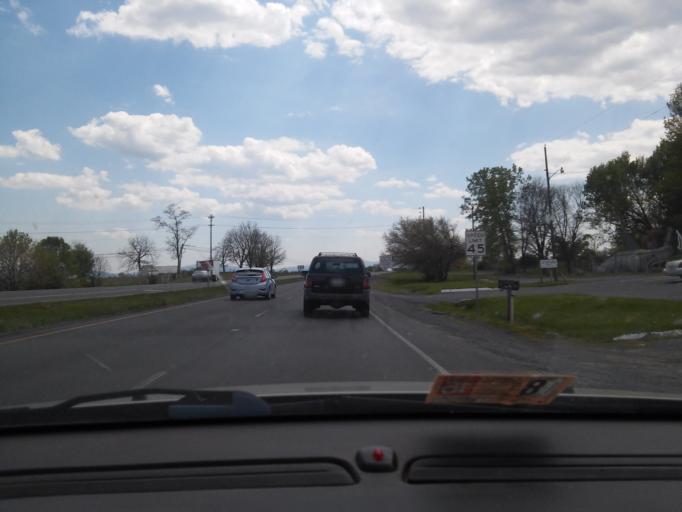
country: US
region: Virginia
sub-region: Frederick County
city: Stephens City
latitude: 39.0602
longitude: -78.1396
